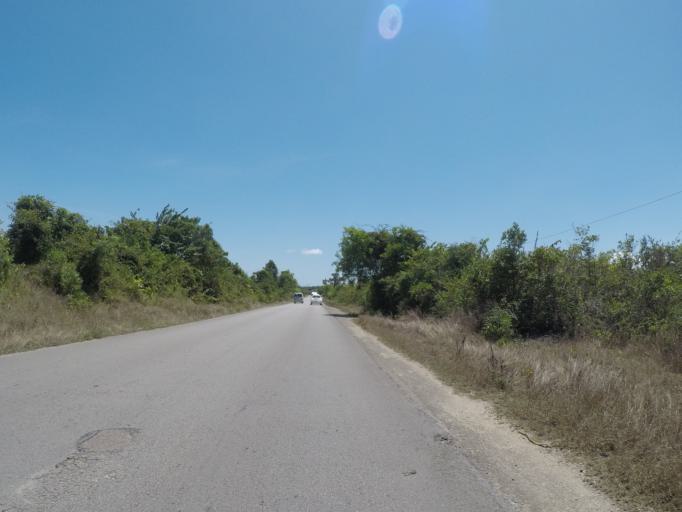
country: TZ
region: Zanzibar Central/South
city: Koani
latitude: -6.2721
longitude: 39.3586
